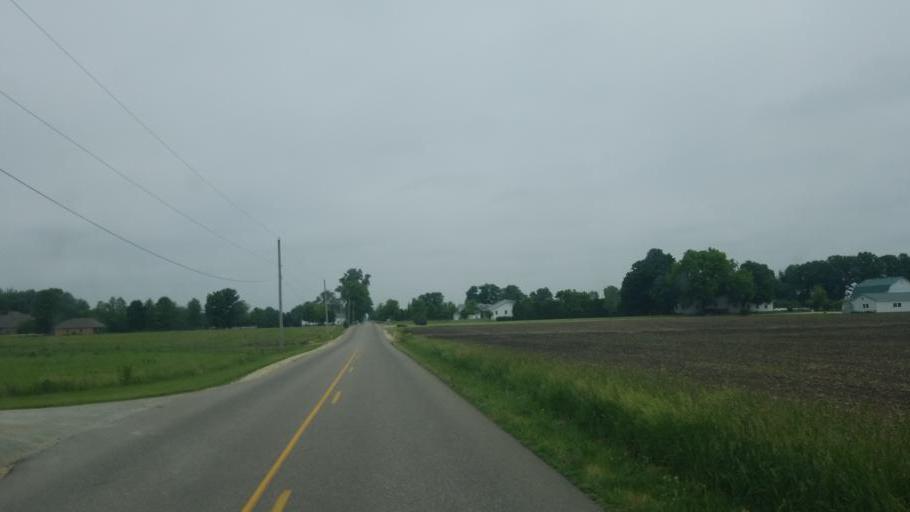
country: US
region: Indiana
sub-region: Elkhart County
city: Nappanee
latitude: 41.4619
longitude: -86.0207
